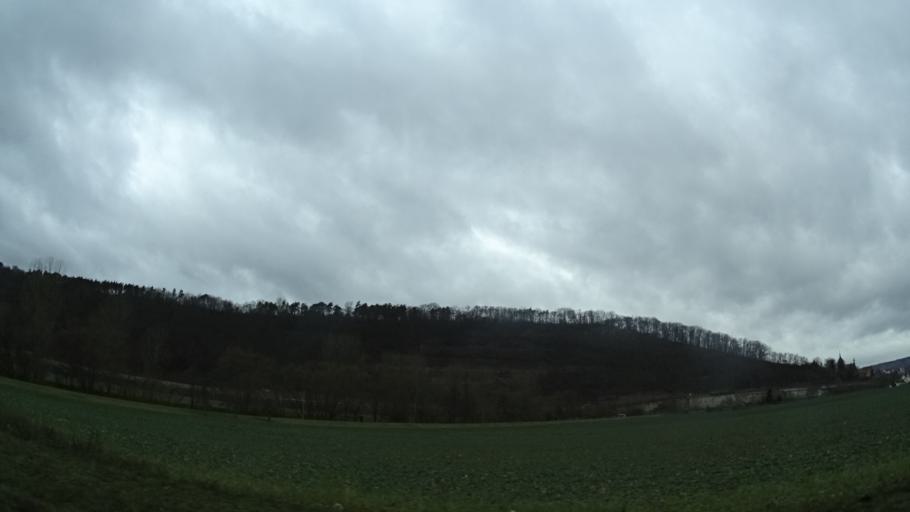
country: DE
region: Thuringia
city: Schops
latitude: 50.8407
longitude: 11.6015
